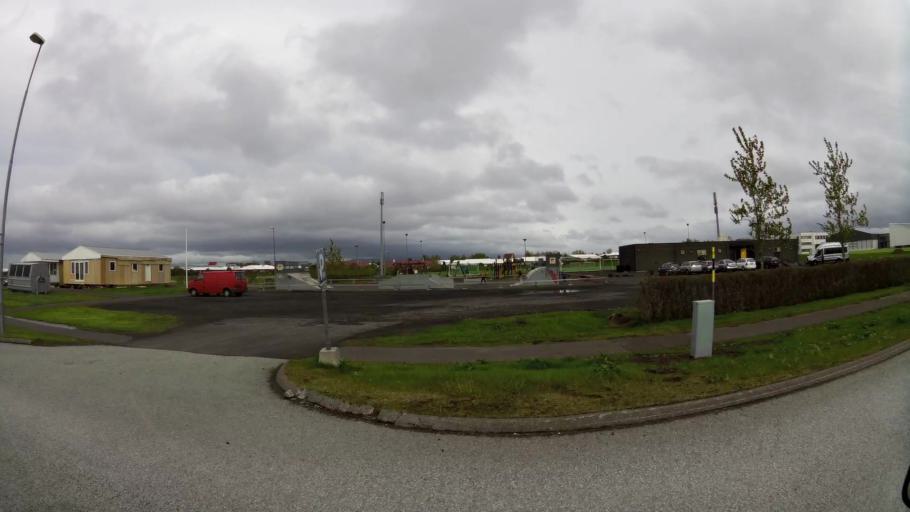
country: IS
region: Capital Region
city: Alftanes
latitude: 64.1050
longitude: -22.0230
